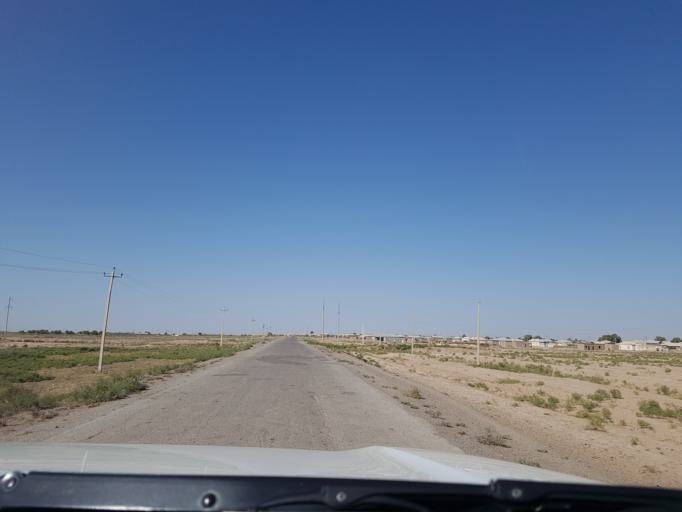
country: IR
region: Razavi Khorasan
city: Sarakhs
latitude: 36.5070
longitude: 61.2534
